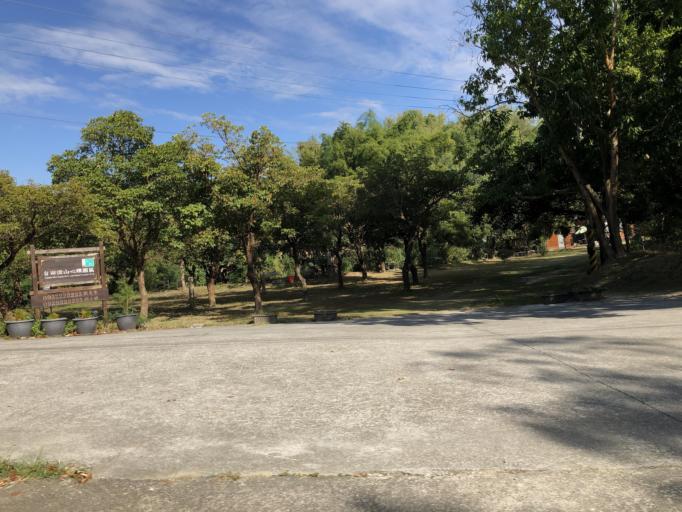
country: TW
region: Taiwan
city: Yujing
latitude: 23.0158
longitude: 120.3983
